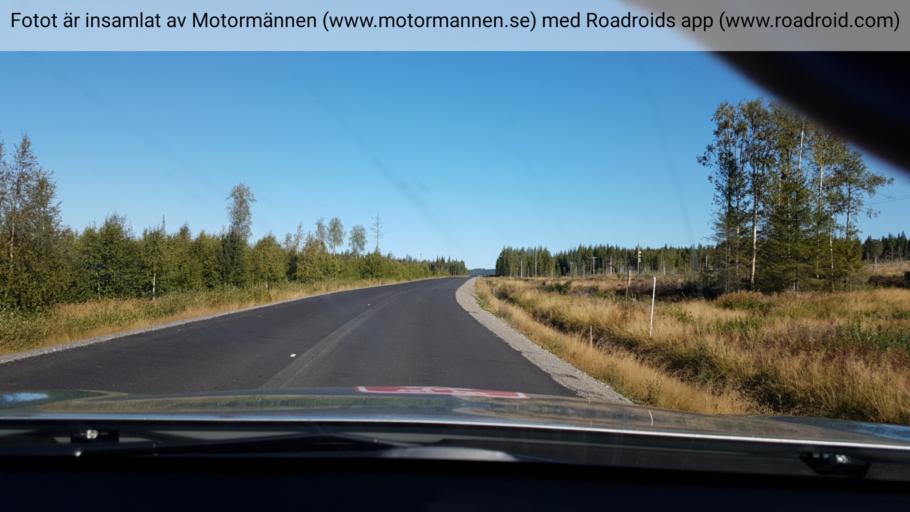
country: SE
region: Vaesterbotten
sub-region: Norsjo Kommun
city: Norsjoe
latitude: 64.8056
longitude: 19.3993
